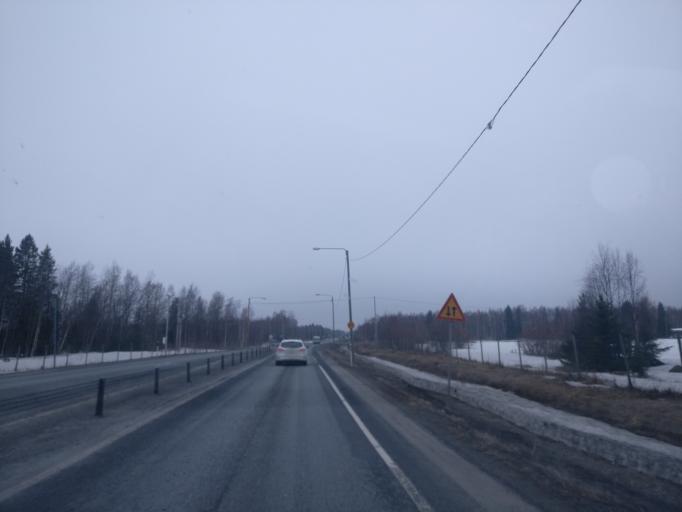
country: FI
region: Lapland
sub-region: Kemi-Tornio
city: Simo
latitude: 65.6691
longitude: 24.9318
